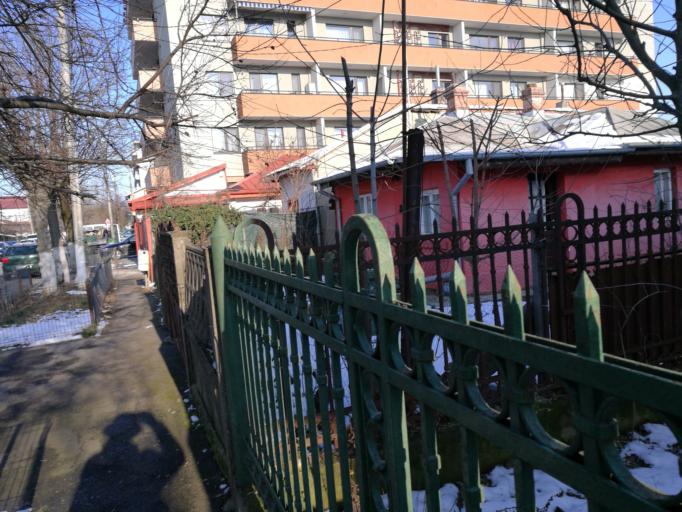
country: RO
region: Ilfov
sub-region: Comuna Otopeni
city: Otopeni
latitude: 44.5059
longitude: 26.0627
